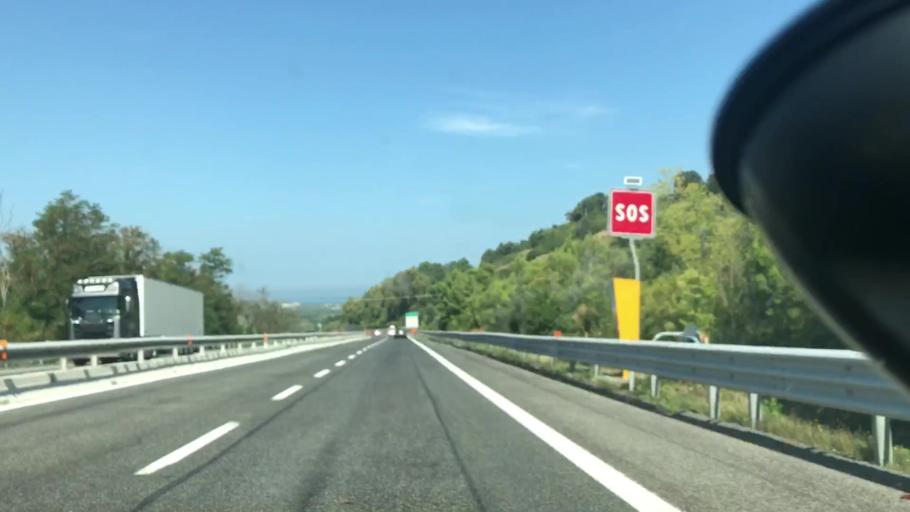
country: IT
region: Abruzzo
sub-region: Provincia di Chieti
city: Vasto
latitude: 42.1443
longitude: 14.6567
